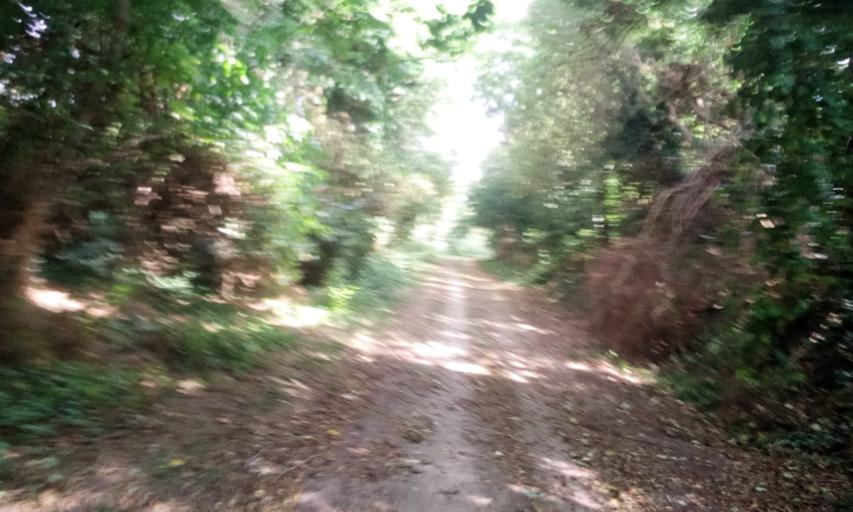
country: FR
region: Lower Normandy
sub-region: Departement du Calvados
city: Douvres-la-Delivrande
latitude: 49.2943
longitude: -0.3988
